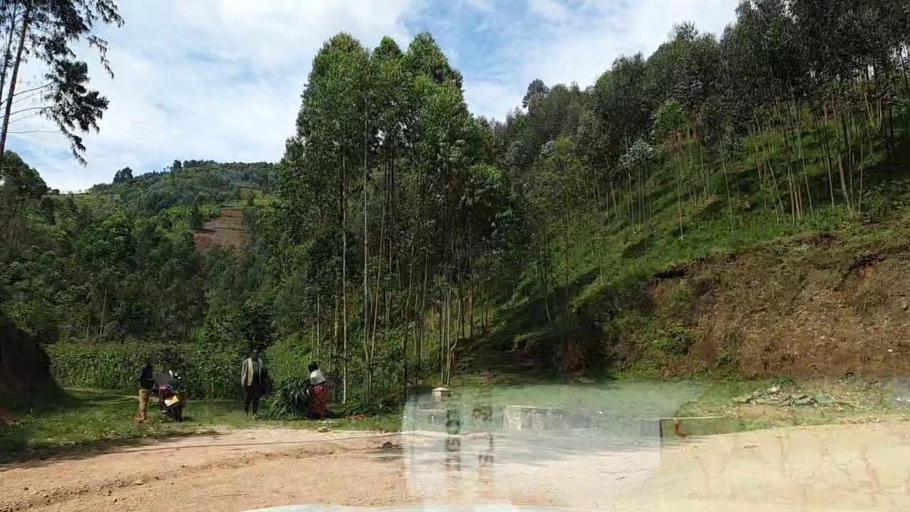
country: RW
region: Southern Province
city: Nzega
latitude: -2.3386
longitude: 29.4383
